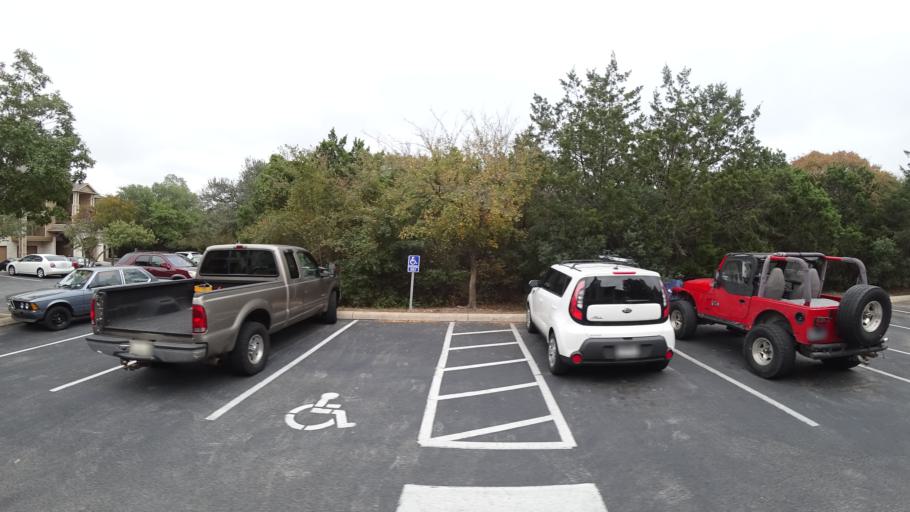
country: US
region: Texas
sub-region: Williamson County
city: Anderson Mill
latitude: 30.4272
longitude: -97.8390
